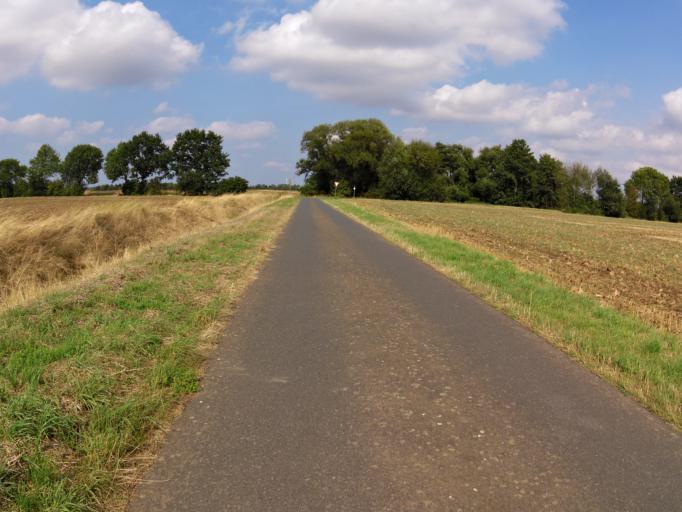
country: DE
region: Lower Saxony
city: Hoya
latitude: 52.8164
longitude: 9.1699
